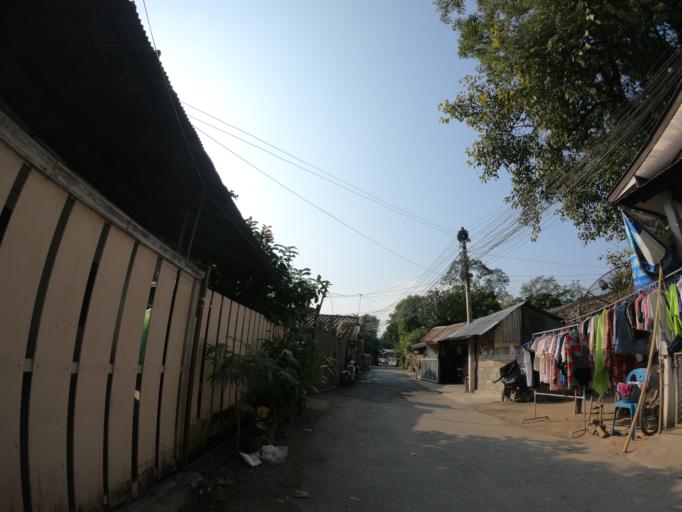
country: TH
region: Chiang Mai
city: Chiang Mai
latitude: 18.7715
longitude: 99.0078
